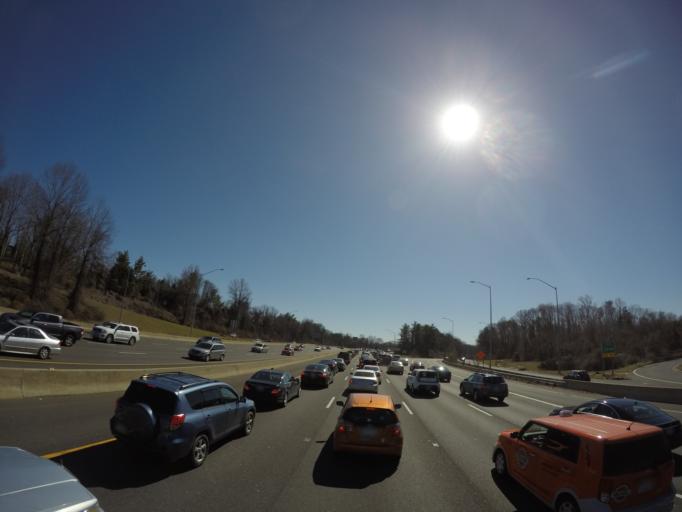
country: US
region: Maryland
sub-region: Montgomery County
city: Cabin John
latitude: 38.9906
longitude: -77.1573
